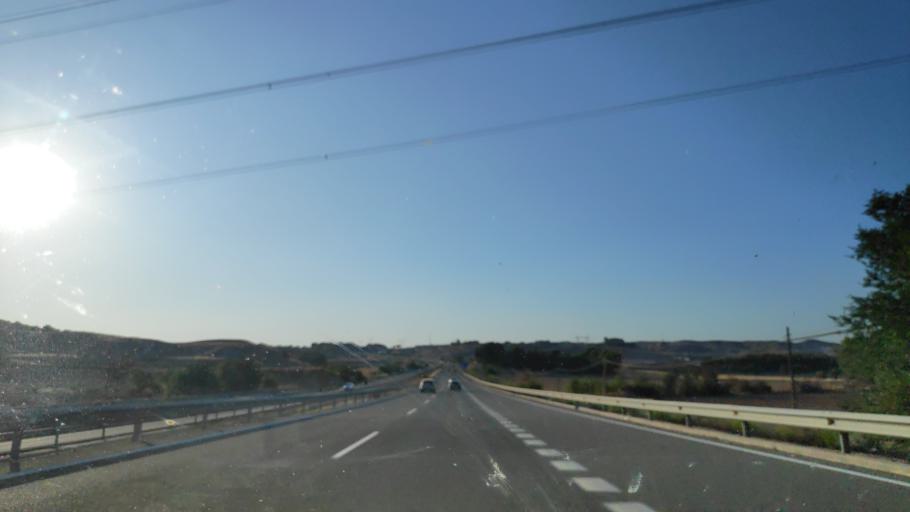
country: ES
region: Castille-La Mancha
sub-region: Provincia de Cuenca
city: Belinchon
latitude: 40.0355
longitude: -3.0454
